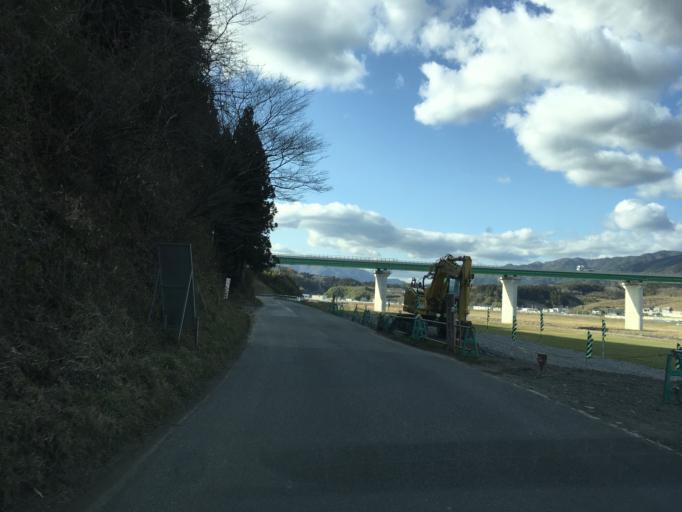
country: JP
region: Iwate
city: Ofunato
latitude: 39.0240
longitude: 141.6160
